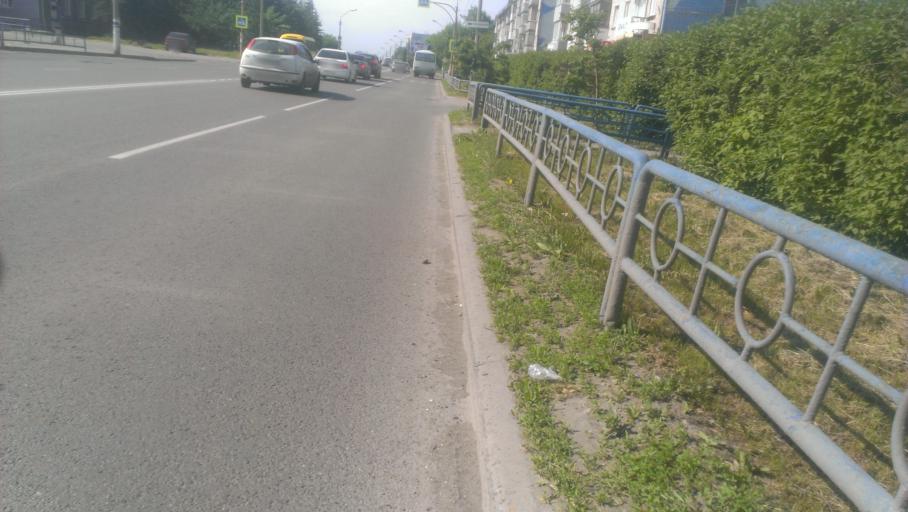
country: RU
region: Altai Krai
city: Novoaltaysk
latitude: 53.3928
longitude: 83.9340
